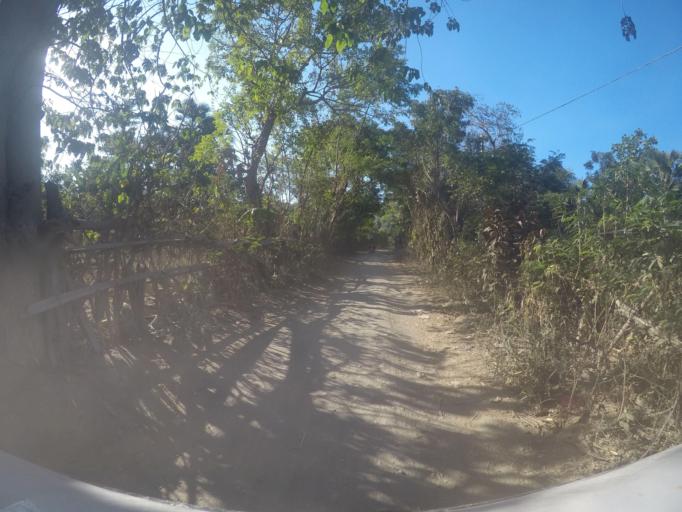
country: ID
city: Metinaro
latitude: -8.5455
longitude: 125.6667
